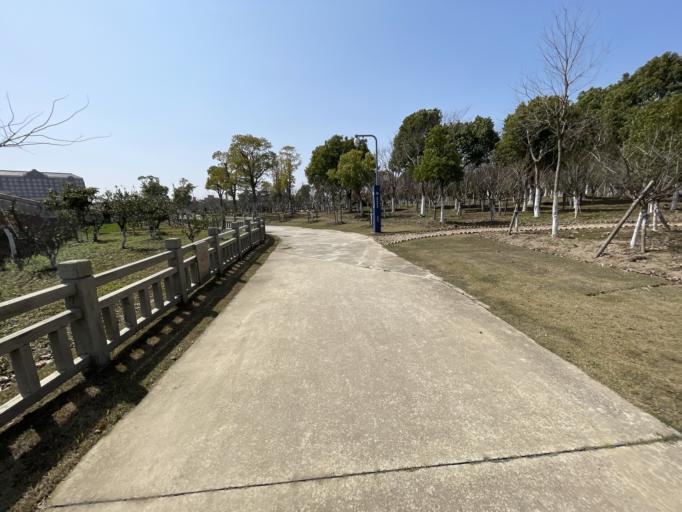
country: CN
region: Shanghai Shi
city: Shuyuan
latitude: 30.8948
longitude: 121.8859
